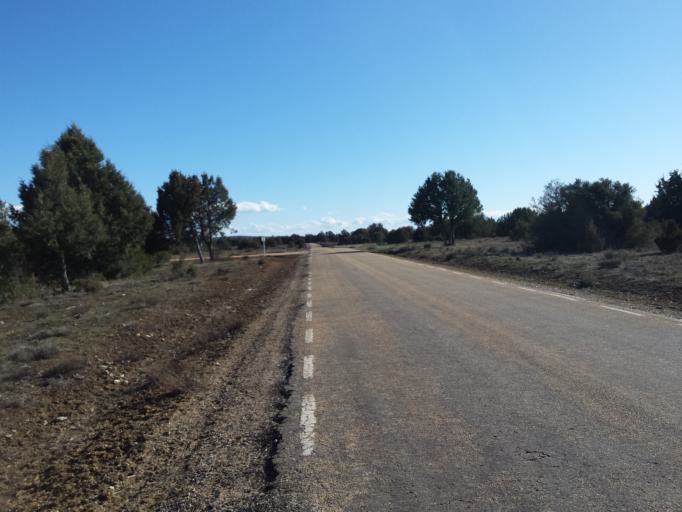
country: ES
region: Castille and Leon
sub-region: Provincia de Soria
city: Calatanazor
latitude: 41.7447
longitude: -2.7757
